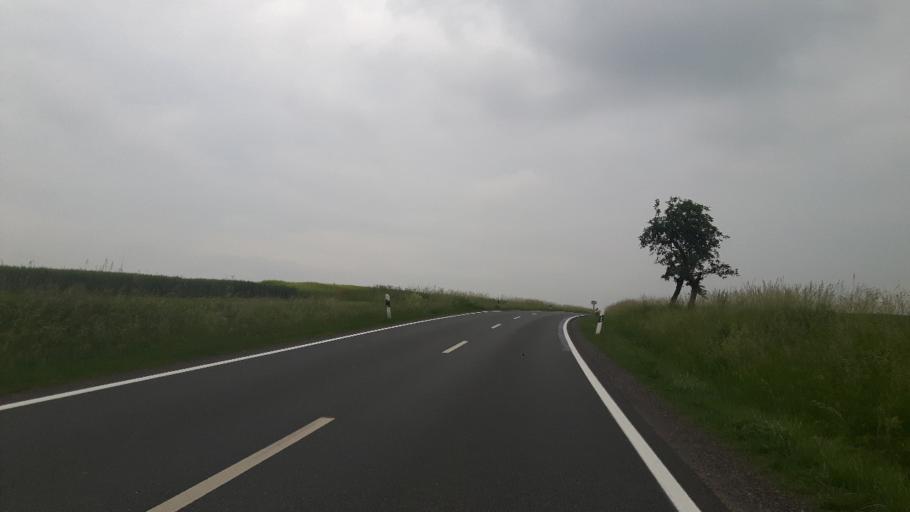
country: DE
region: Bavaria
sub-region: Regierungsbezirk Unterfranken
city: Schwanfeld
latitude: 49.9031
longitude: 10.1263
